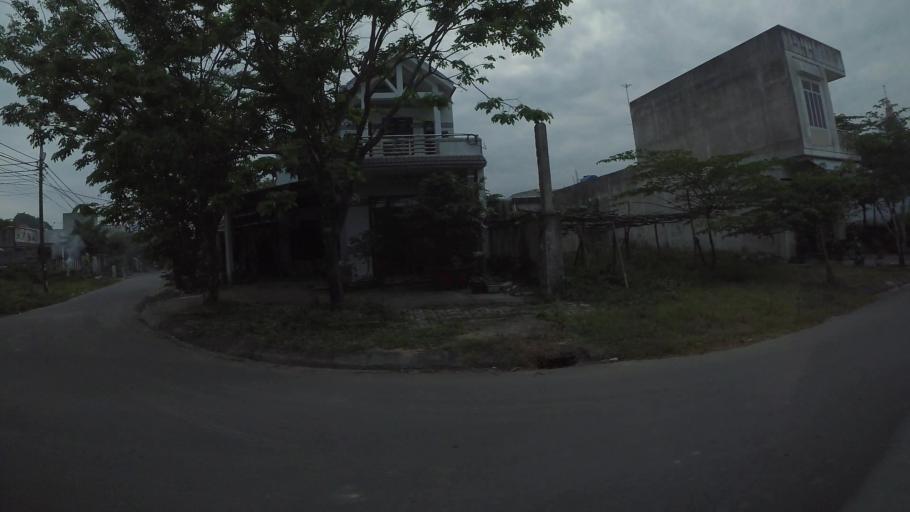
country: VN
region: Da Nang
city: Lien Chieu
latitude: 16.0669
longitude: 108.1045
